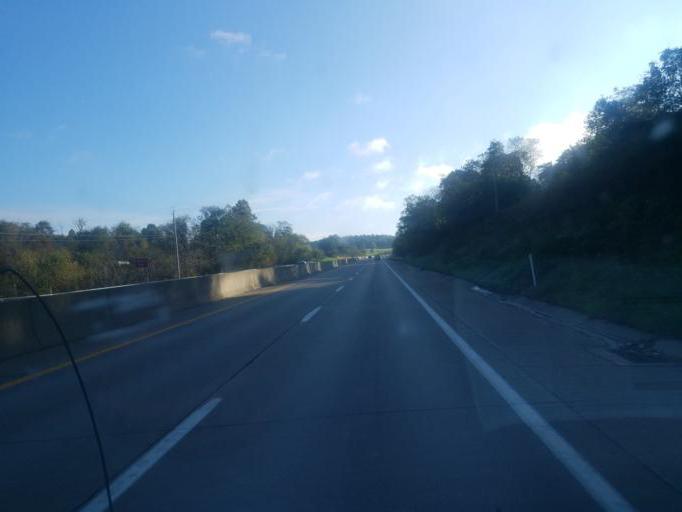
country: US
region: Pennsylvania
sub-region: Westmoreland County
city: Delmont
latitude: 40.4028
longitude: -79.5465
